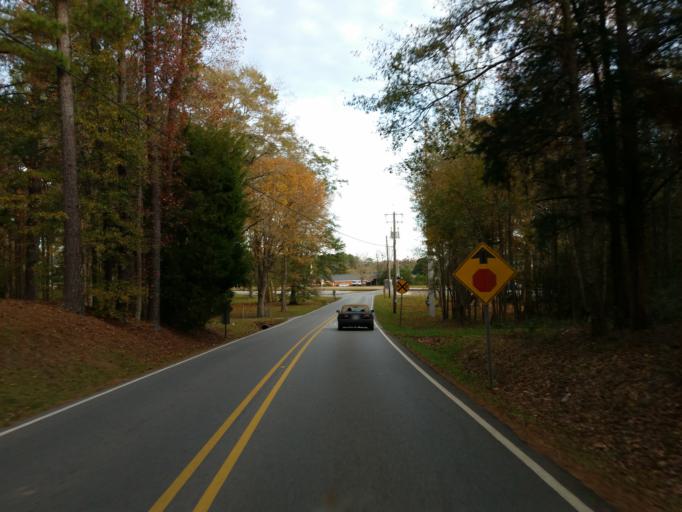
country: US
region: Mississippi
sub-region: Lauderdale County
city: Marion
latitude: 32.4036
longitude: -88.5979
